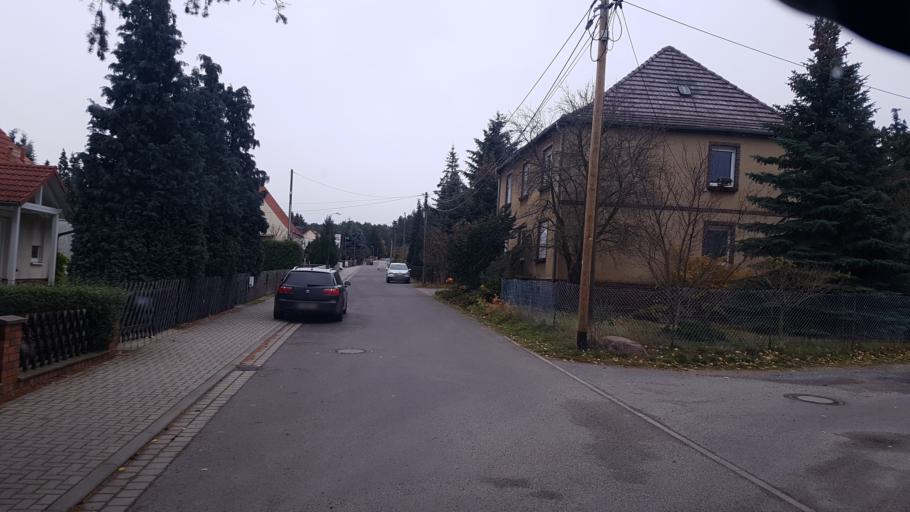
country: DE
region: Brandenburg
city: Crinitz
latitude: 51.7379
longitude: 13.7665
